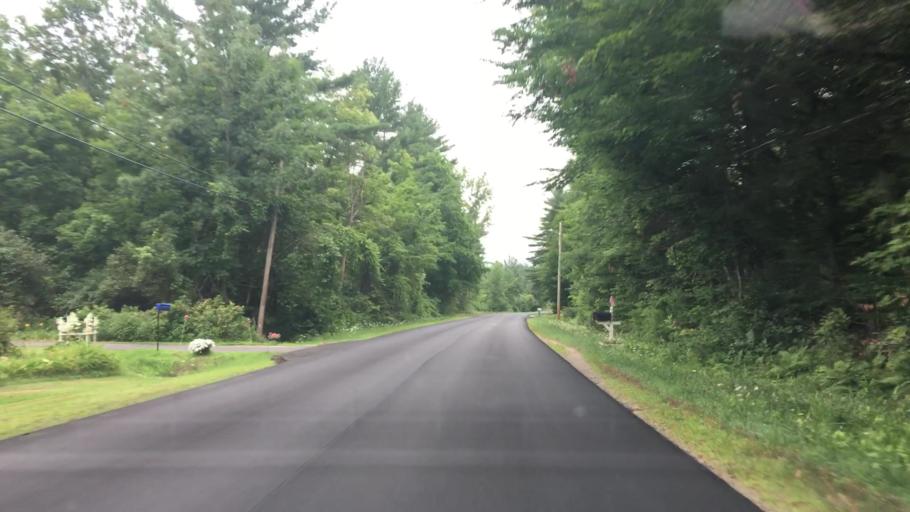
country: US
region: New York
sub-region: Clinton County
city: Peru
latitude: 44.5803
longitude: -73.5701
